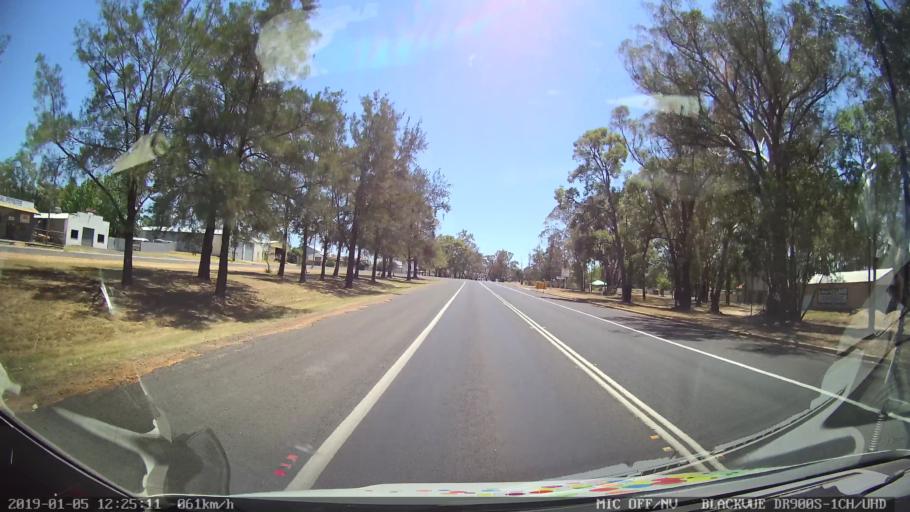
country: AU
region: New South Wales
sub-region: Warrumbungle Shire
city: Coonabarabran
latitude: -31.2627
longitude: 149.2844
